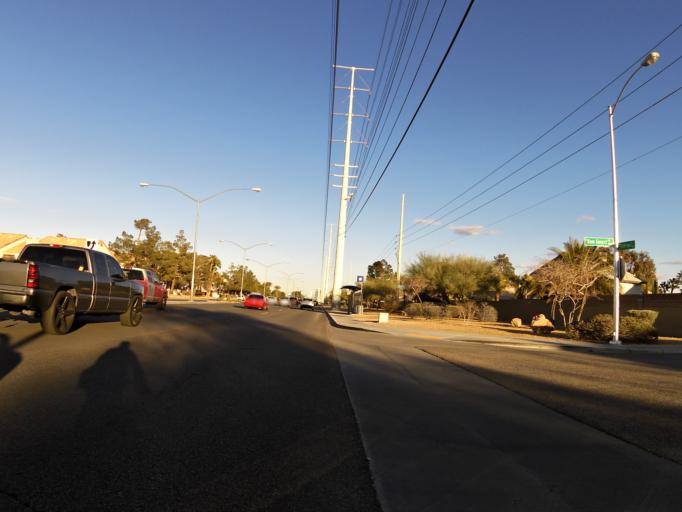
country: US
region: Nevada
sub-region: Clark County
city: Spring Valley
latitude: 36.1145
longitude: -115.2572
